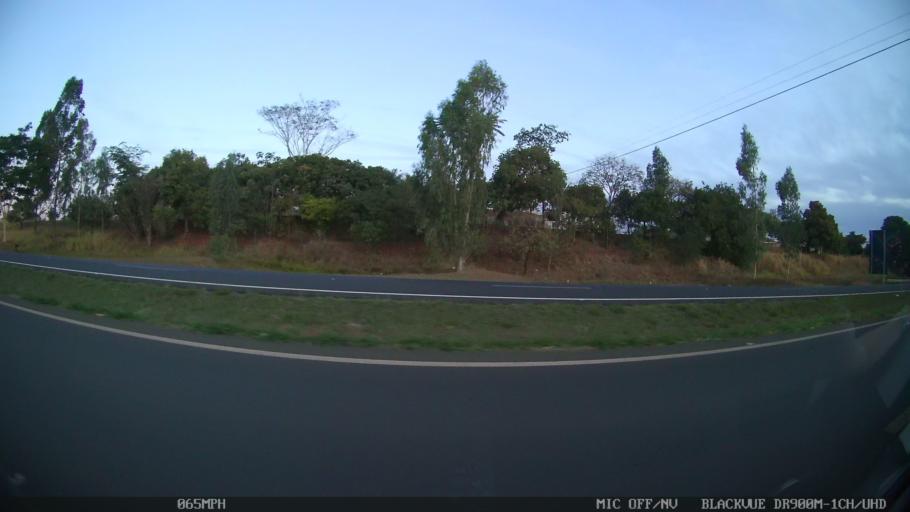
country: BR
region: Sao Paulo
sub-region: Catanduva
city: Catanduva
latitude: -21.1115
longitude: -48.9690
